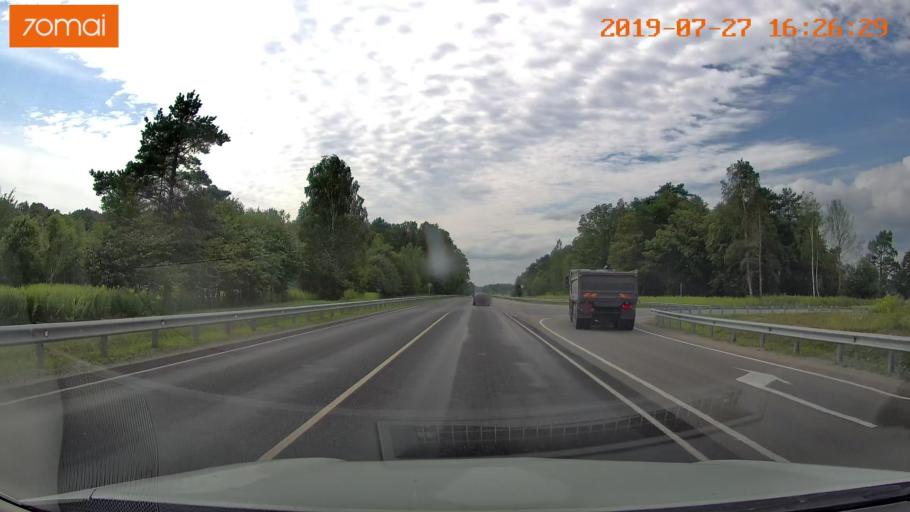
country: RU
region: Kaliningrad
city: Zheleznodorozhnyy
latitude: 54.6405
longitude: 21.4094
